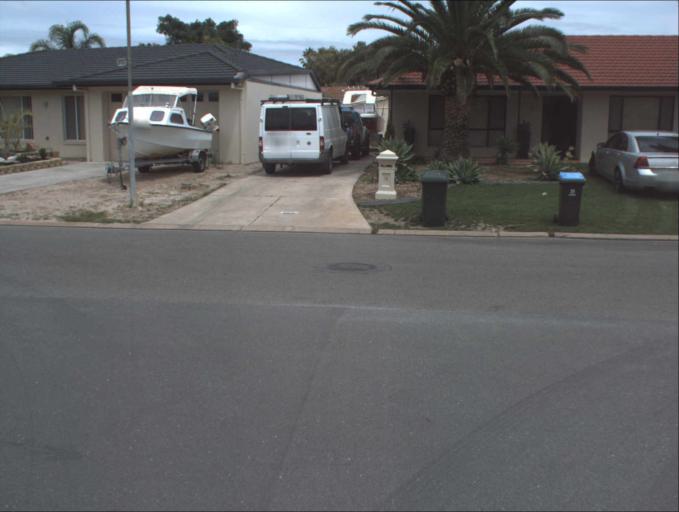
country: AU
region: South Australia
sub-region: Port Adelaide Enfield
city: Birkenhead
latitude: -34.7884
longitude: 138.4960
